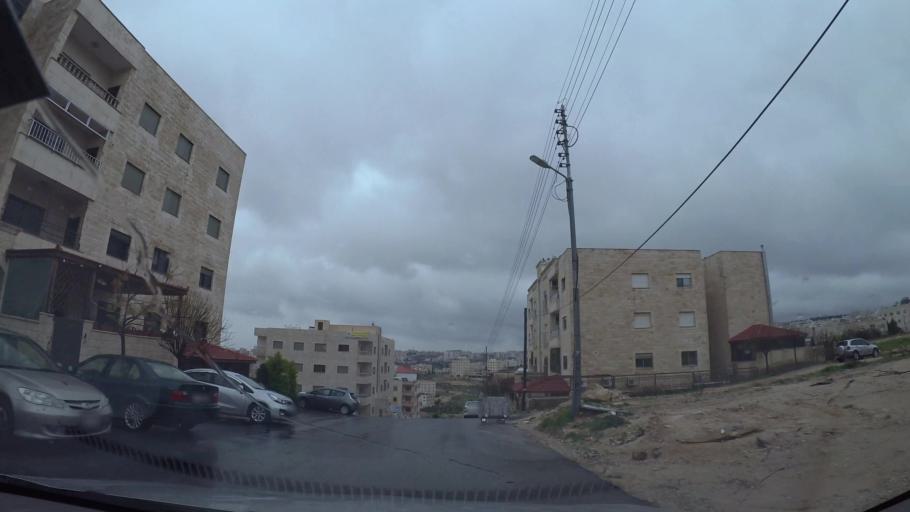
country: JO
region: Amman
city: Al Jubayhah
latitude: 32.0429
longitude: 35.8904
